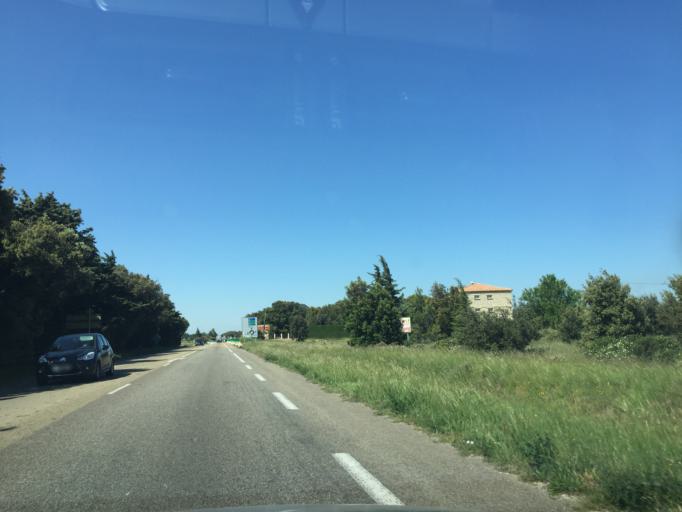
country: FR
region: Languedoc-Roussillon
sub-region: Departement du Gard
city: Saze
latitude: 43.9519
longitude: 4.6410
